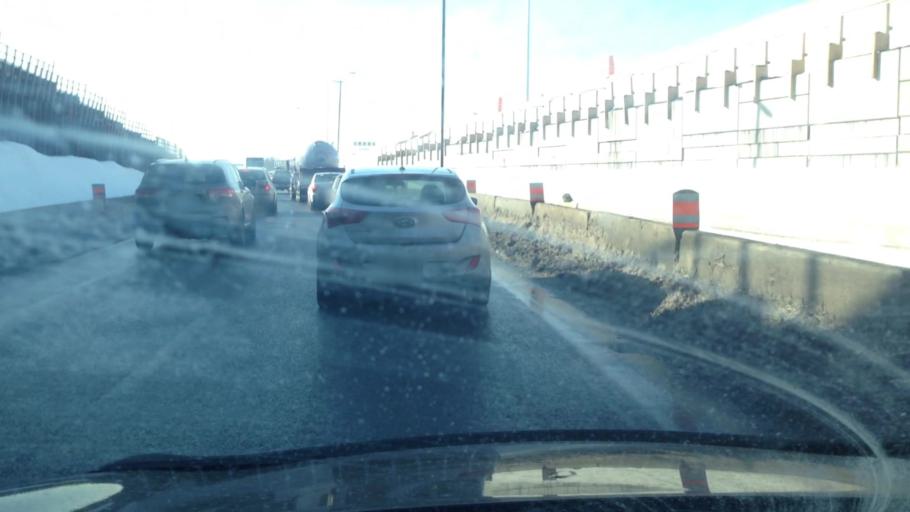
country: CA
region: Quebec
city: Montreal-Ouest
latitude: 45.4505
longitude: -73.6332
